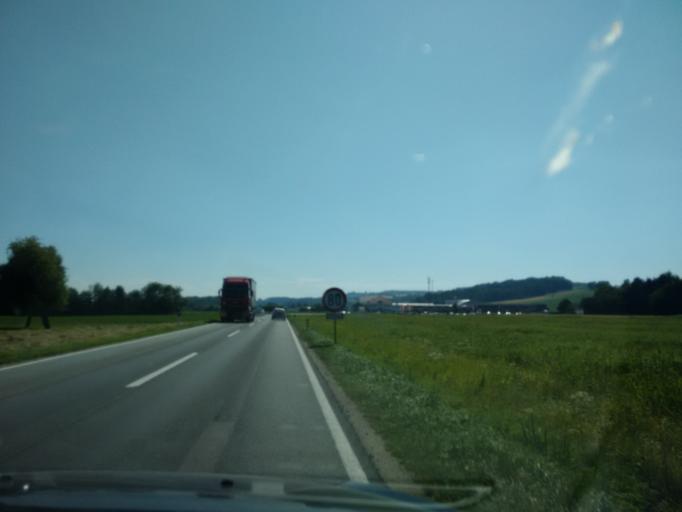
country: AT
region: Upper Austria
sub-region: Wels-Land
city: Buchkirchen
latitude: 48.2734
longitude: 13.9937
